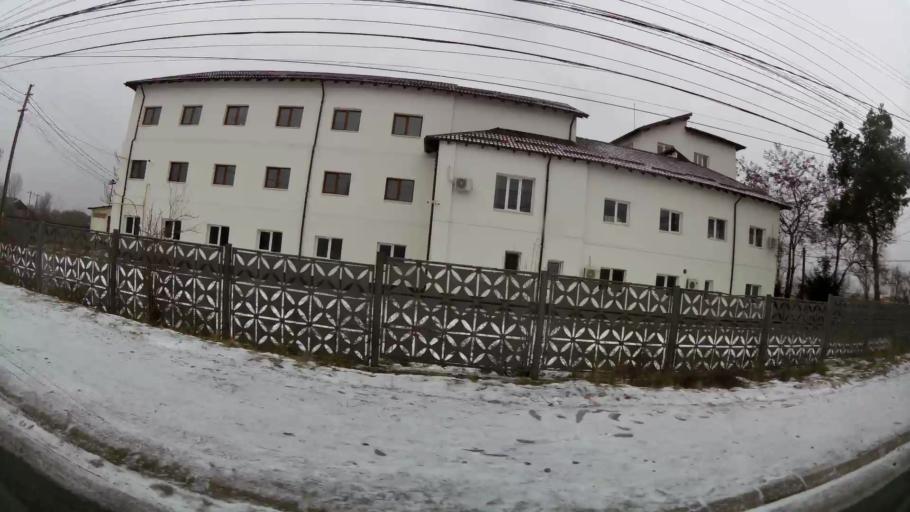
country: RO
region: Dambovita
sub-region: Municipiul Targoviste
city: Targoviste
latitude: 44.9319
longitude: 25.4749
